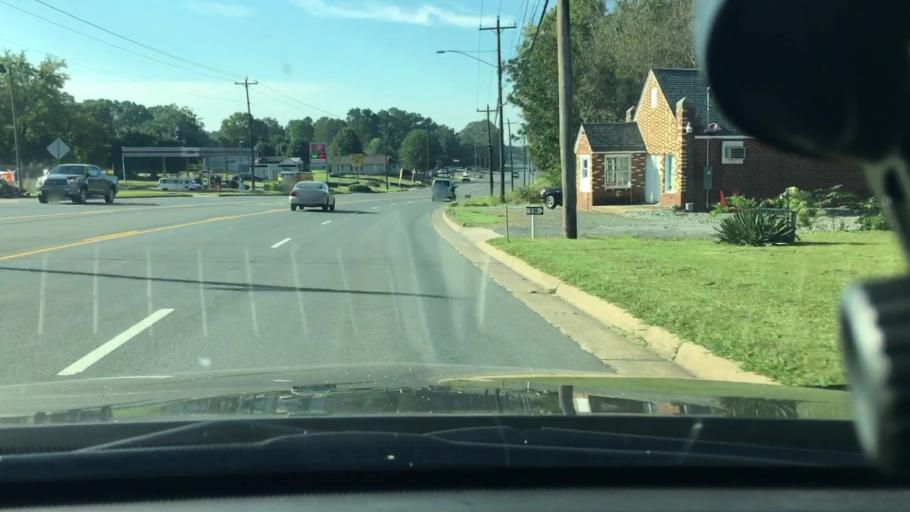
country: US
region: North Carolina
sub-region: Stanly County
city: Albemarle
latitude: 35.3837
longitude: -80.1930
